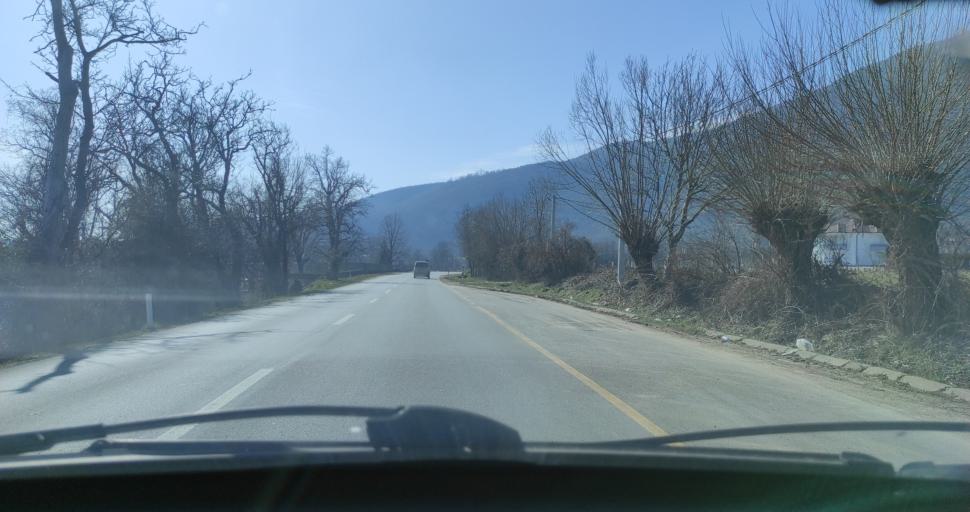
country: XK
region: Gjakova
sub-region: Komuna e Decanit
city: Strellc i Eperm
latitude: 42.5974
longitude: 20.2968
